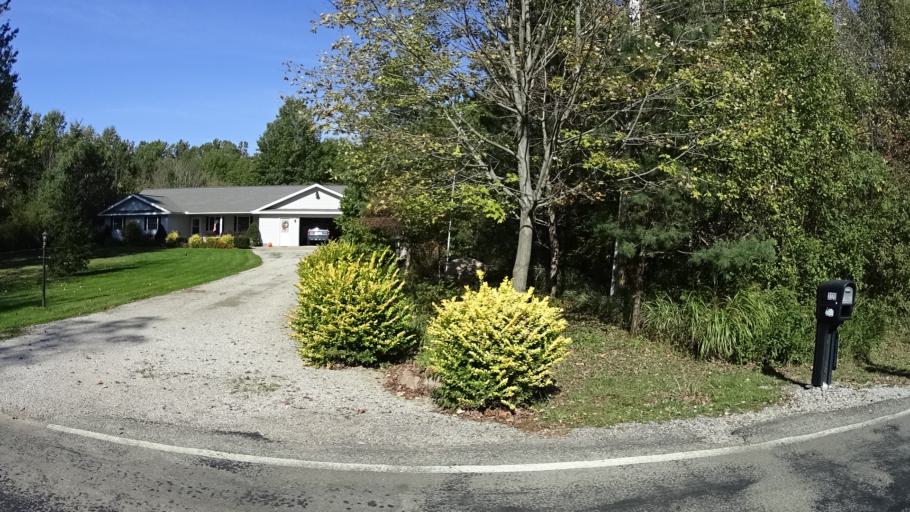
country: US
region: Ohio
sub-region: Lorain County
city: Vermilion-on-the-Lake
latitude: 41.4117
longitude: -82.3131
